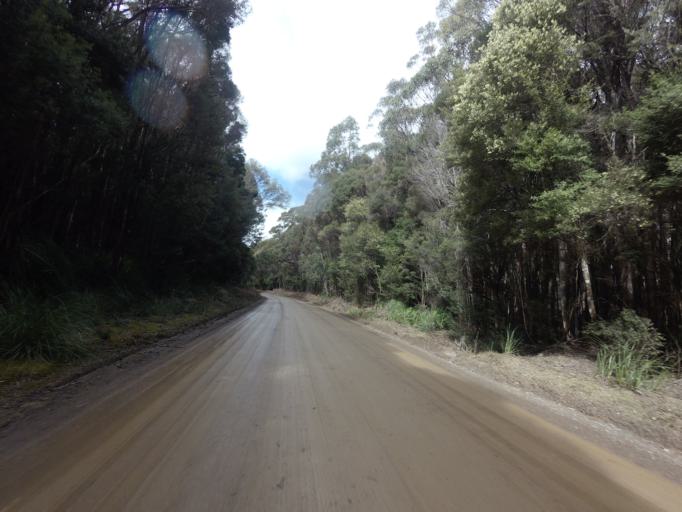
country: AU
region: Tasmania
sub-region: Huon Valley
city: Geeveston
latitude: -43.4048
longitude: 146.8669
